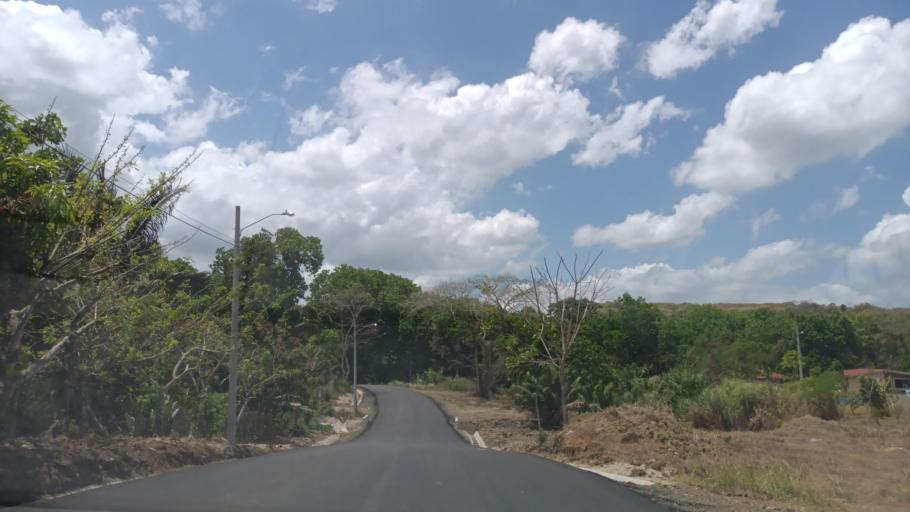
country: PA
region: Panama
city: Alcalde Diaz
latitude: 9.0970
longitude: -79.5746
